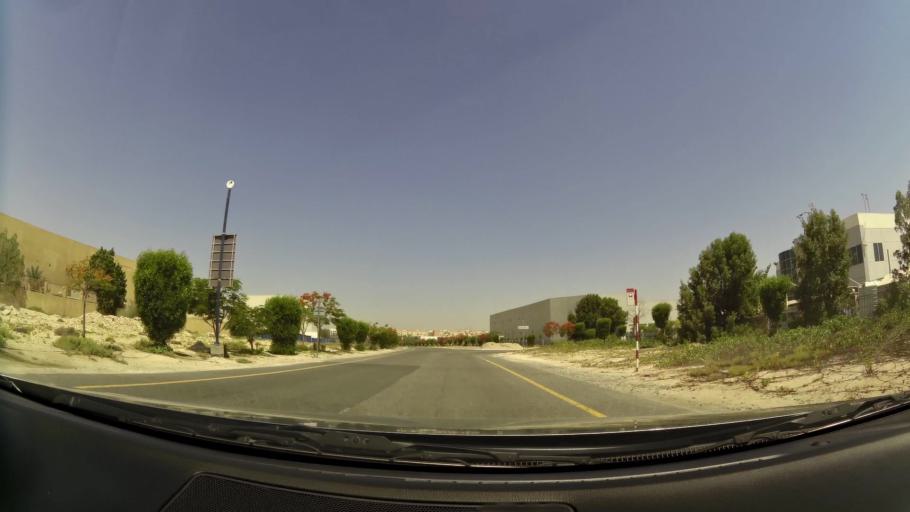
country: AE
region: Dubai
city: Dubai
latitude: 24.9838
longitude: 55.2117
